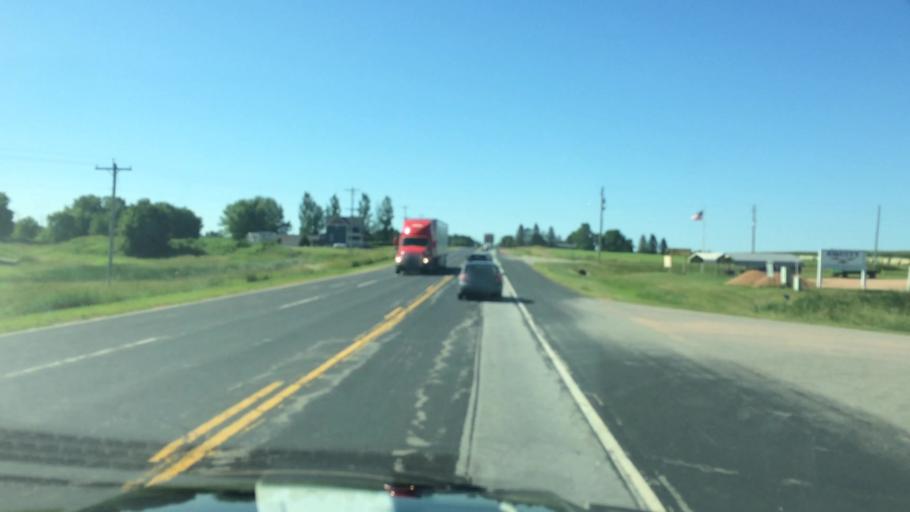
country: US
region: Wisconsin
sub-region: Marathon County
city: Stratford
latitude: 44.8199
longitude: -90.0791
